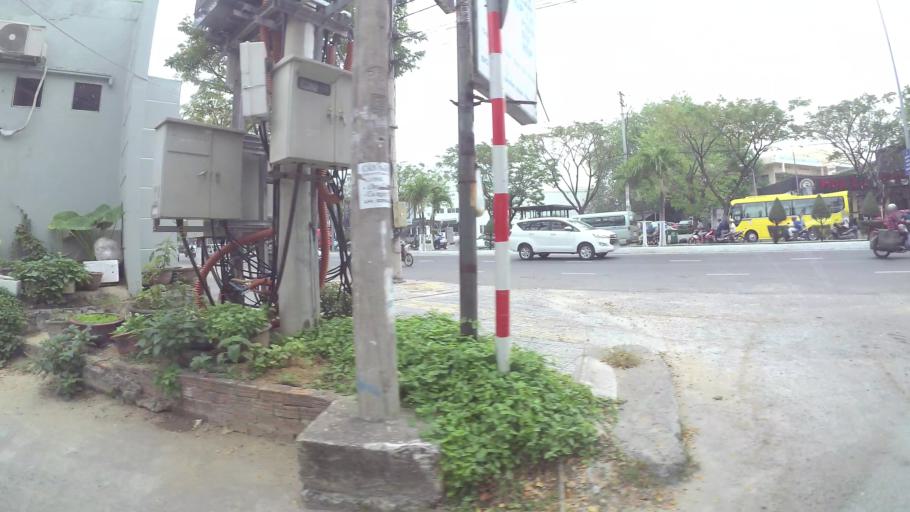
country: VN
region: Da Nang
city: Da Nang
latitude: 16.0484
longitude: 108.2092
